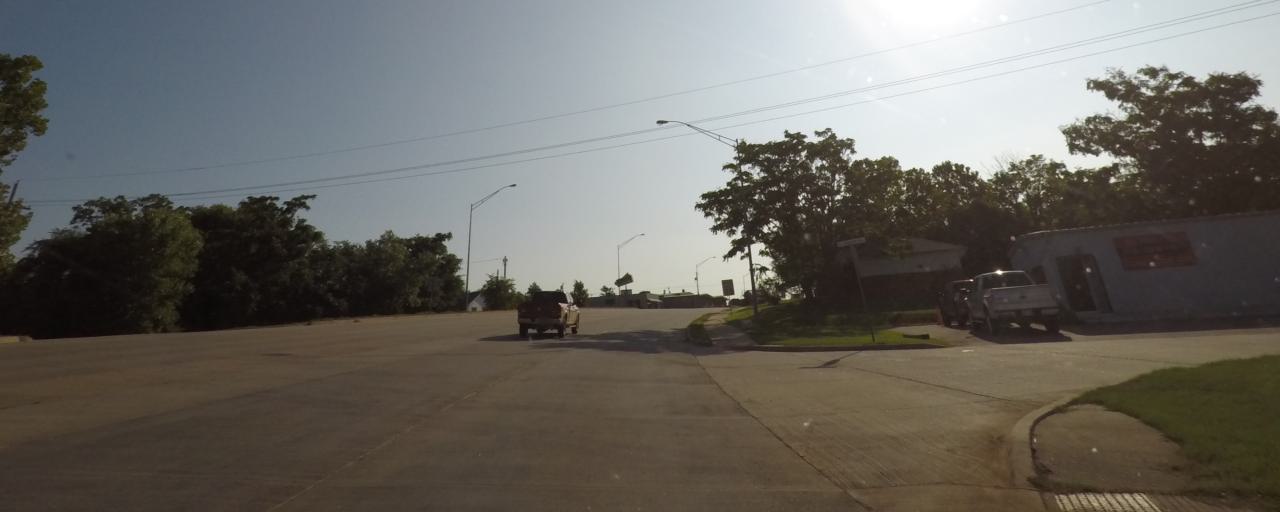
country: US
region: Oklahoma
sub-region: McClain County
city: Blanchard
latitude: 35.1377
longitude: -97.6622
